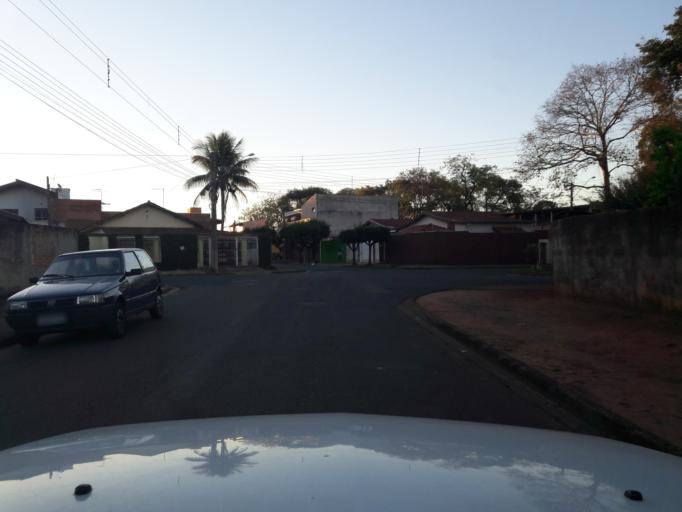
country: BR
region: Sao Paulo
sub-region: Moji-Guacu
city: Mogi-Gaucu
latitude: -22.3390
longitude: -46.9323
